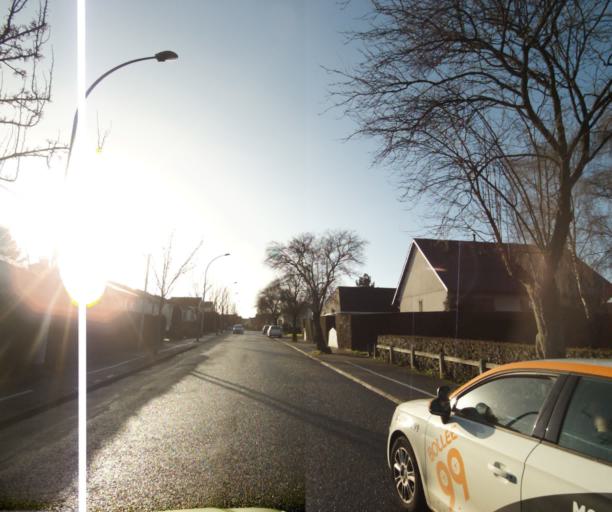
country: FR
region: Pays de la Loire
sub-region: Departement de la Sarthe
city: Sarge-les-le-Mans
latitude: 48.0170
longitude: 0.2274
